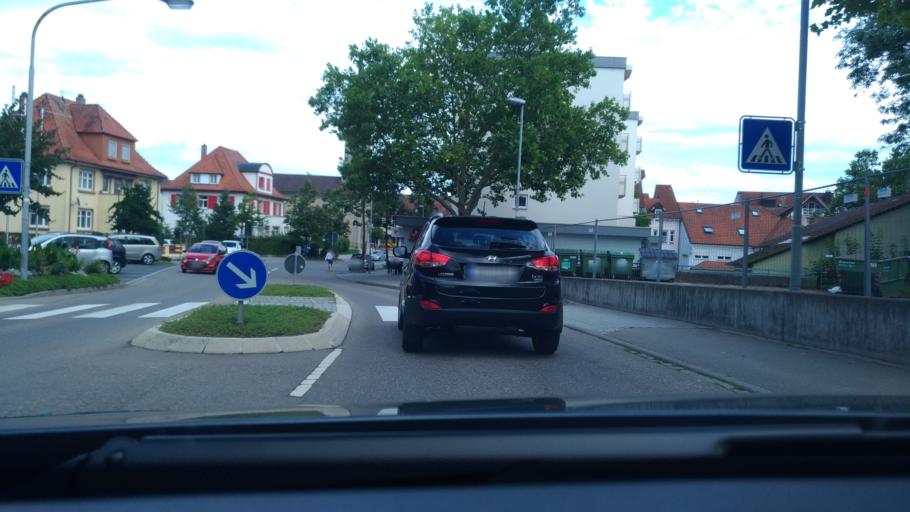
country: DE
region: Baden-Wuerttemberg
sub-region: Freiburg Region
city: Stockach
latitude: 47.8546
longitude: 9.0131
